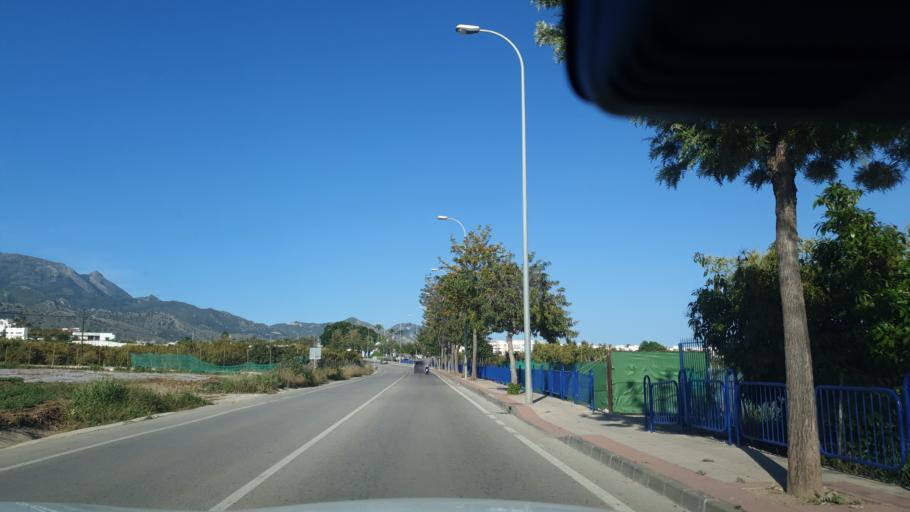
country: ES
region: Andalusia
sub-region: Provincia de Malaga
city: Nerja
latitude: 36.7471
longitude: -3.8883
